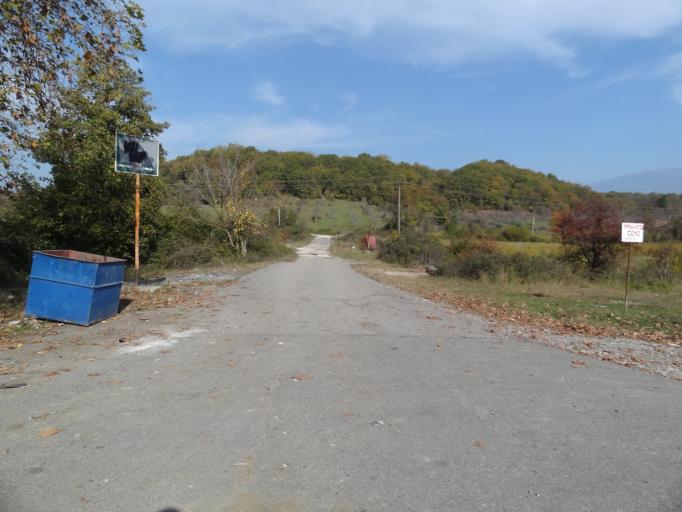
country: GE
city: Gantiadi
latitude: 43.3903
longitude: 40.0344
